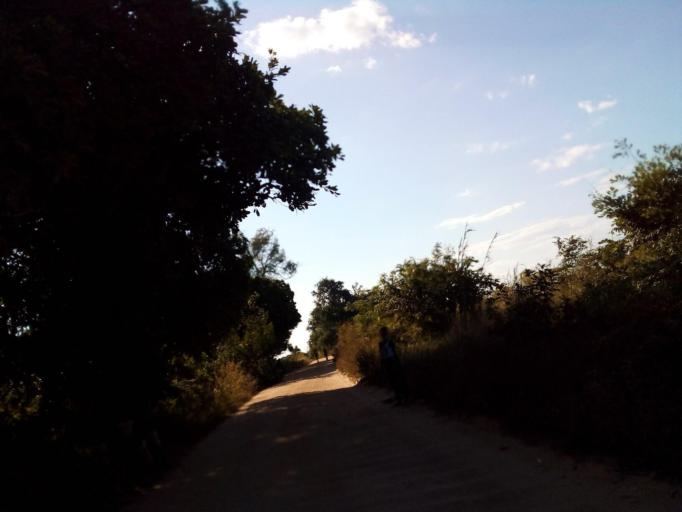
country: MZ
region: Zambezia
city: Quelimane
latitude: -17.5317
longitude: 36.6199
